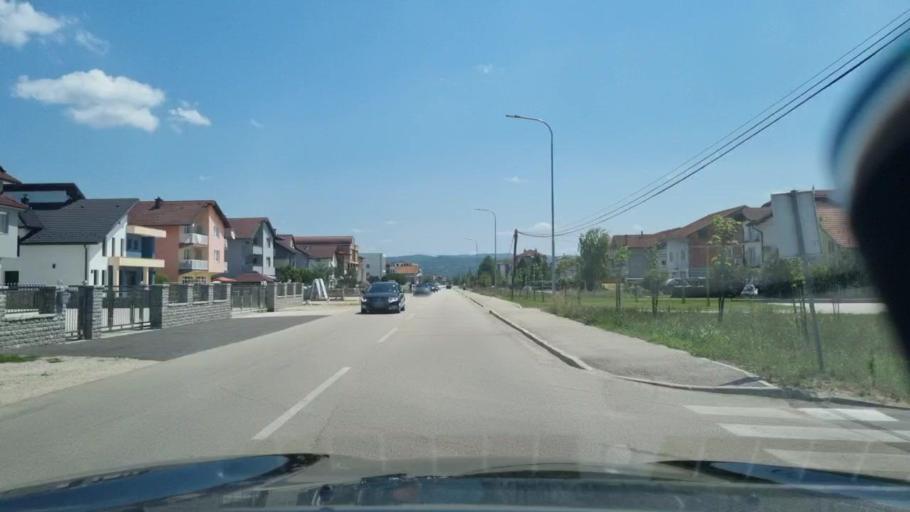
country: BA
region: Federation of Bosnia and Herzegovina
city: Sanski Most
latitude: 44.7710
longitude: 16.6501
